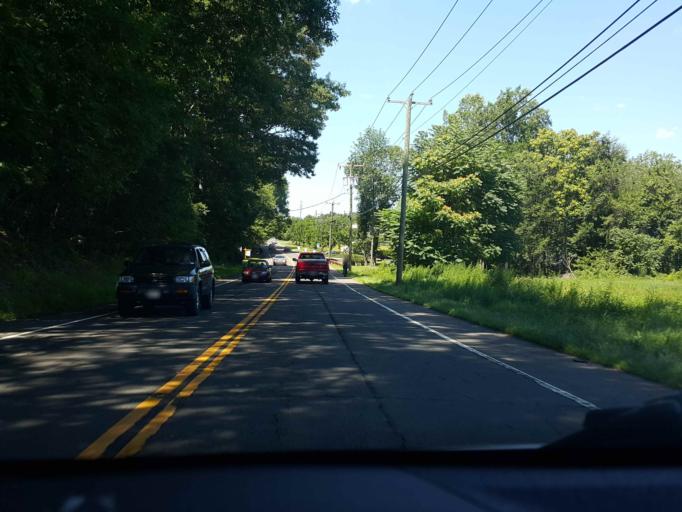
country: US
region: Connecticut
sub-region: New Haven County
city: Guilford
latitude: 41.2933
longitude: -72.6990
